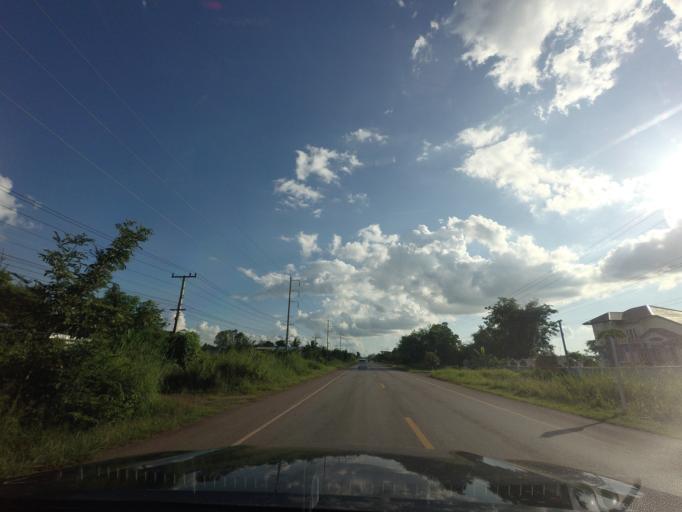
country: TH
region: Changwat Udon Thani
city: Thung Fon
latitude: 17.4978
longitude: 103.2021
